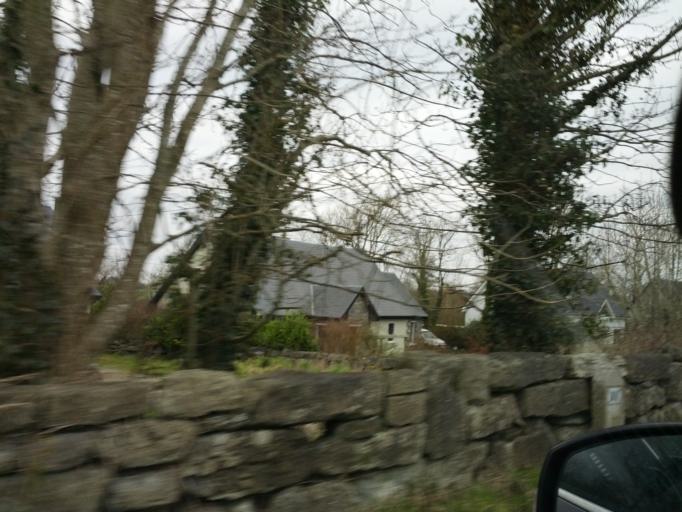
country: IE
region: Connaught
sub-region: County Galway
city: Oranmore
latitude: 53.1900
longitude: -8.9181
